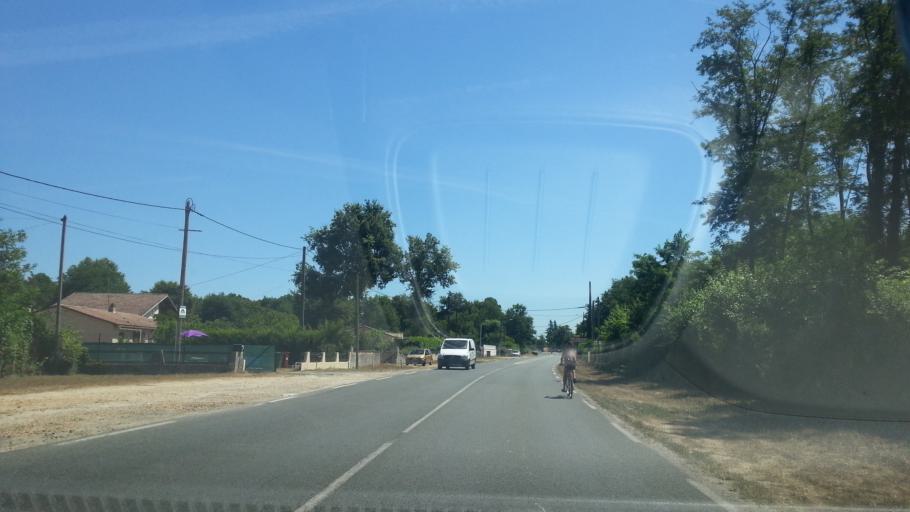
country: FR
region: Aquitaine
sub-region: Departement de la Gironde
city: Illats
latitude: 44.5619
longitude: -0.3647
